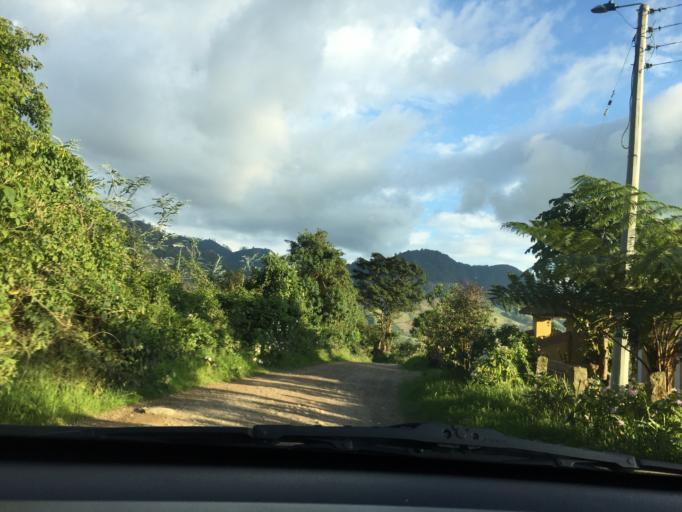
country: CO
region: Cundinamarca
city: Zipacon
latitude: 4.7381
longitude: -74.3855
